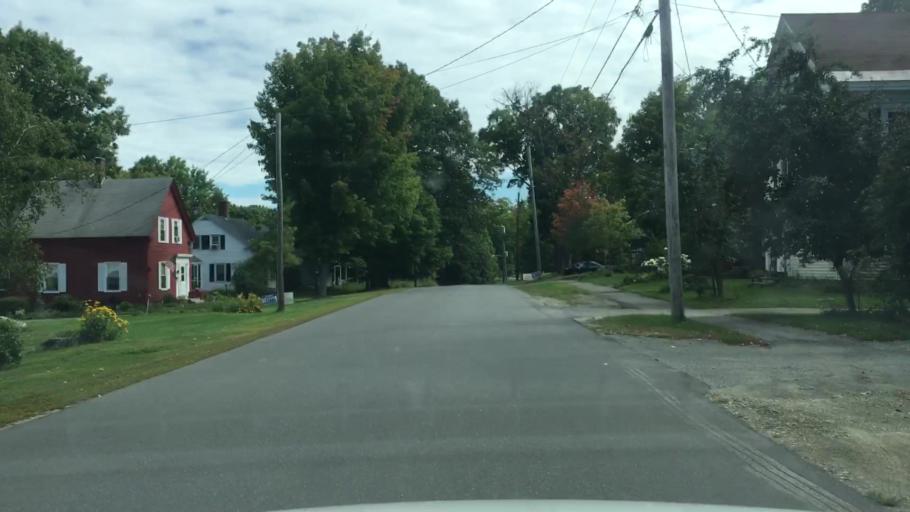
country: US
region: Maine
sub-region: Piscataquis County
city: Dover-Foxcroft
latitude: 45.1853
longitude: -69.2274
